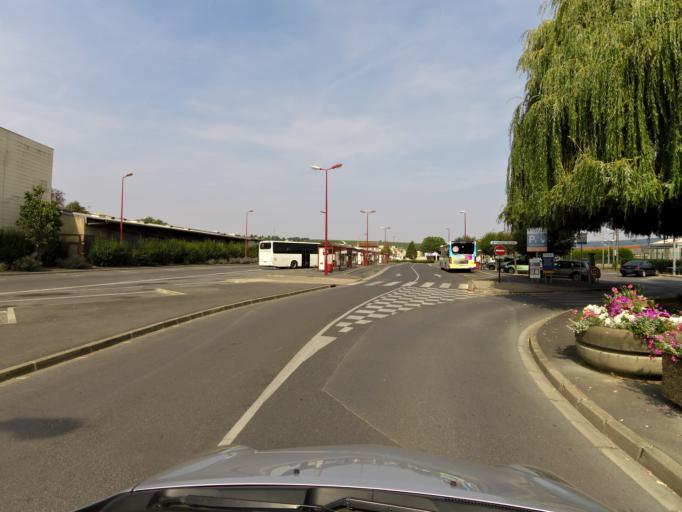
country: FR
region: Champagne-Ardenne
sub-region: Departement de la Marne
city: Epernay
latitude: 49.0464
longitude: 3.9591
